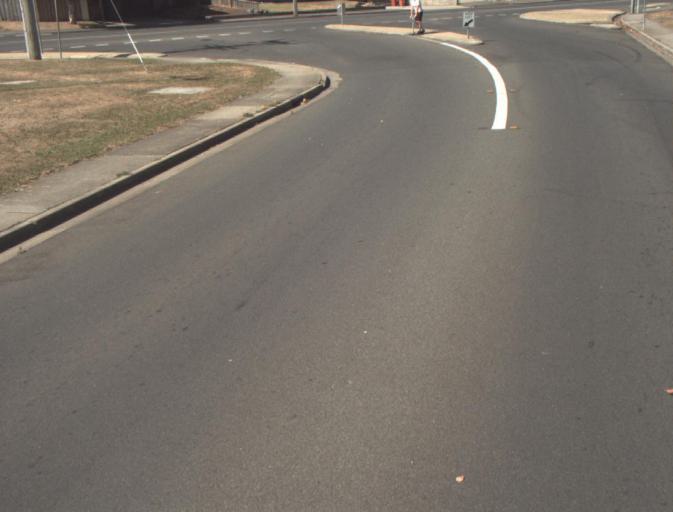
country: AU
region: Tasmania
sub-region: Launceston
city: Newstead
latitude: -41.4187
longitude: 147.1744
